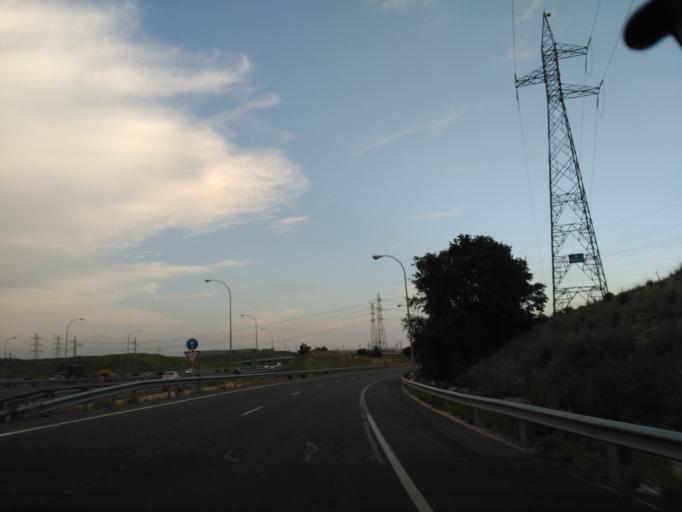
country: ES
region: Madrid
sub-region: Provincia de Madrid
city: Villaverde
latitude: 40.3317
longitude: -3.6767
